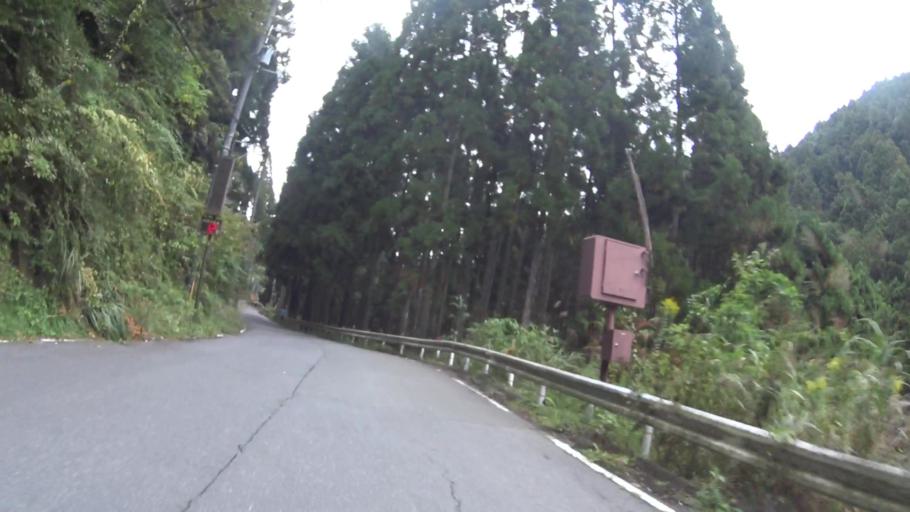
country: JP
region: Kyoto
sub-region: Kyoto-shi
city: Kamigyo-ku
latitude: 35.1232
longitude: 135.7763
